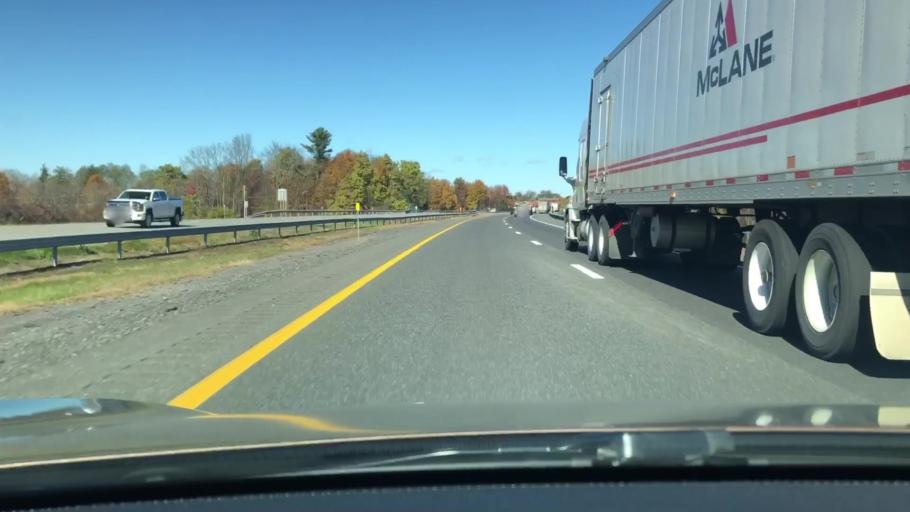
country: US
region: New York
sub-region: Ulster County
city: Plattekill
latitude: 41.5854
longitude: -74.0888
